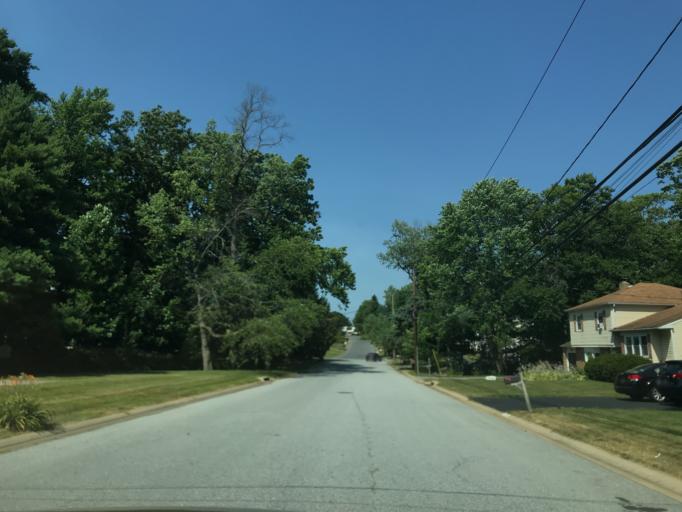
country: US
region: Delaware
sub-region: New Castle County
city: Claymont
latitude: 39.8312
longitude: -75.5148
